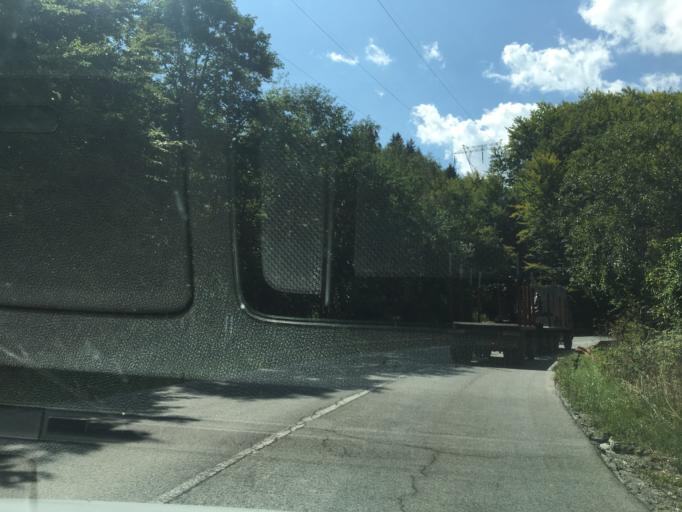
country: RS
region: Central Serbia
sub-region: Zlatiborski Okrug
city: Prijepolje
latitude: 43.3270
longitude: 19.5416
